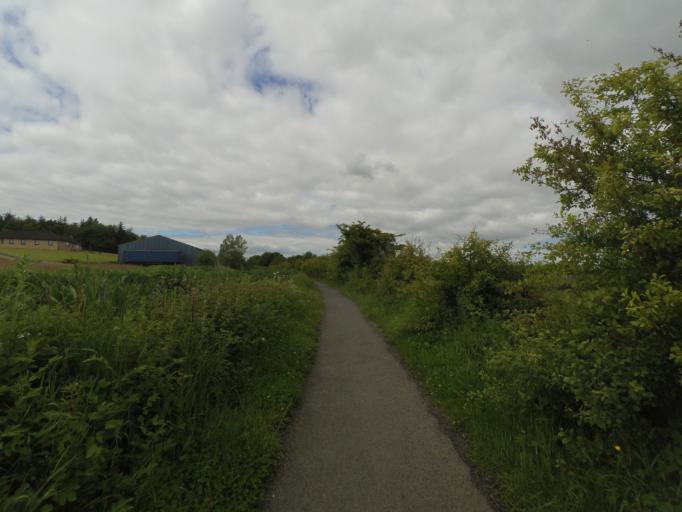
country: GB
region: Scotland
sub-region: Falkirk
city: Polmont
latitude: 55.9784
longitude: -3.6812
